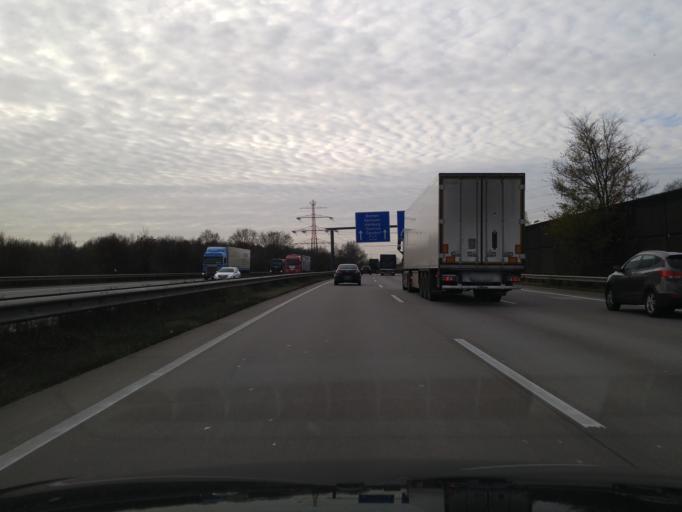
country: DE
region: Schleswig-Holstein
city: Barsbuettel
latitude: 53.5667
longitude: 10.1881
